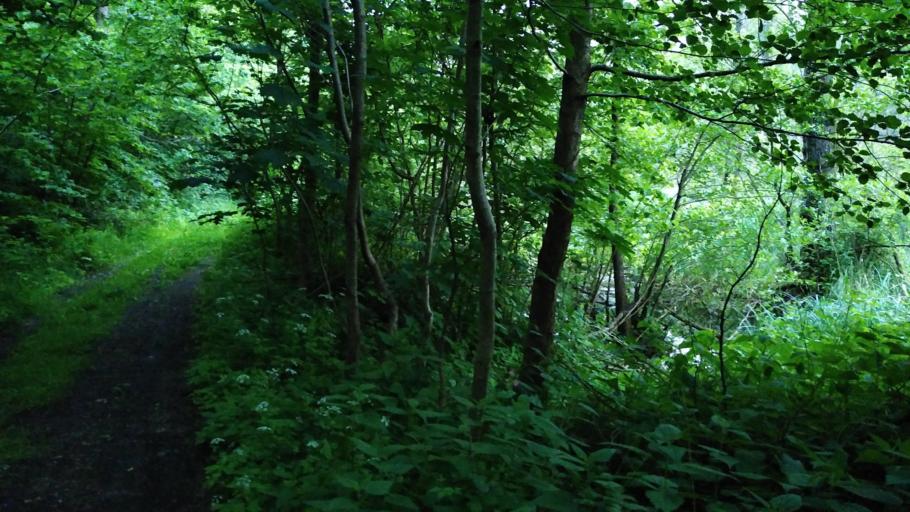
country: DE
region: Schleswig-Holstein
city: Kabelhorst
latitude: 54.2337
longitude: 10.9166
